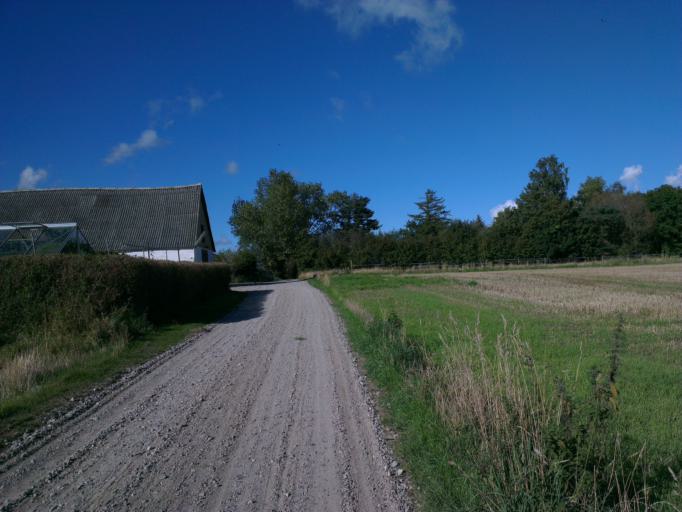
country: DK
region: Capital Region
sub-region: Frederikssund Kommune
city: Frederikssund
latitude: 55.7907
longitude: 12.0430
